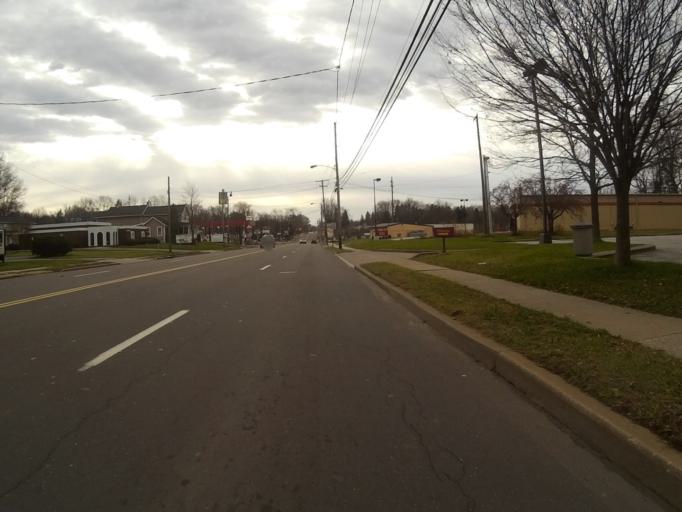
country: US
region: Ohio
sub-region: Portage County
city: Kent
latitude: 41.1426
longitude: -81.3579
